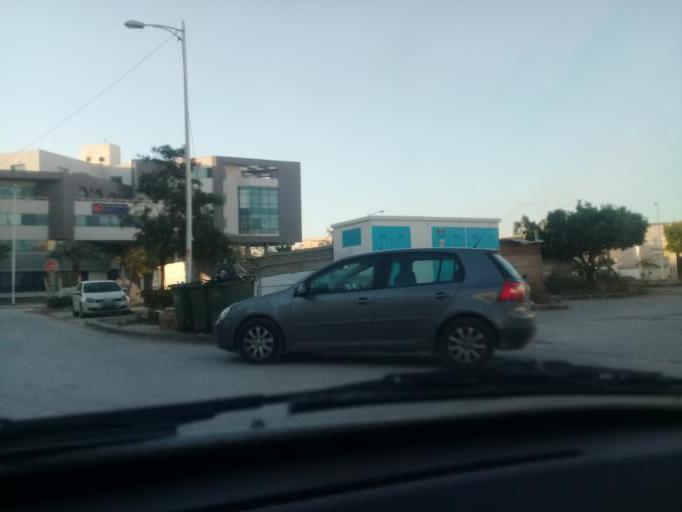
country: TN
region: Tunis
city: La Goulette
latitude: 36.8458
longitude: 10.2712
